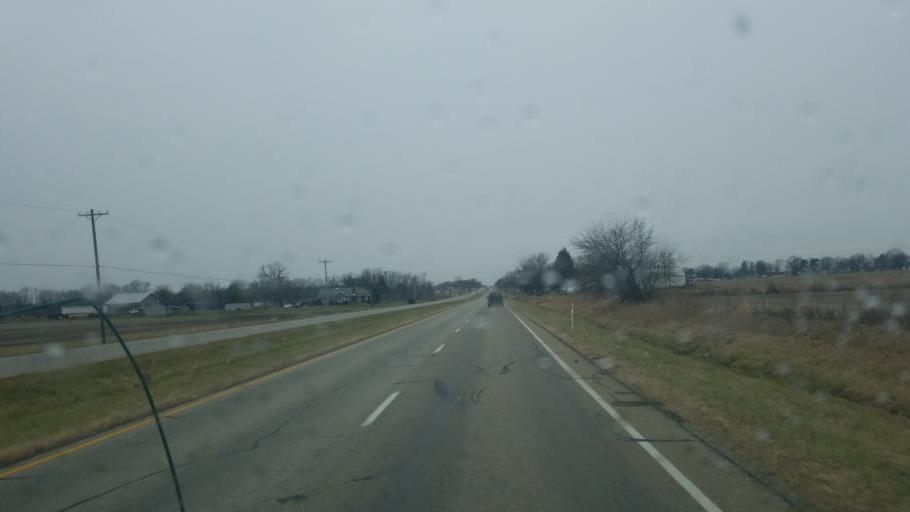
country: US
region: Indiana
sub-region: Hancock County
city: Greenfield
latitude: 39.7892
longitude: -85.6798
